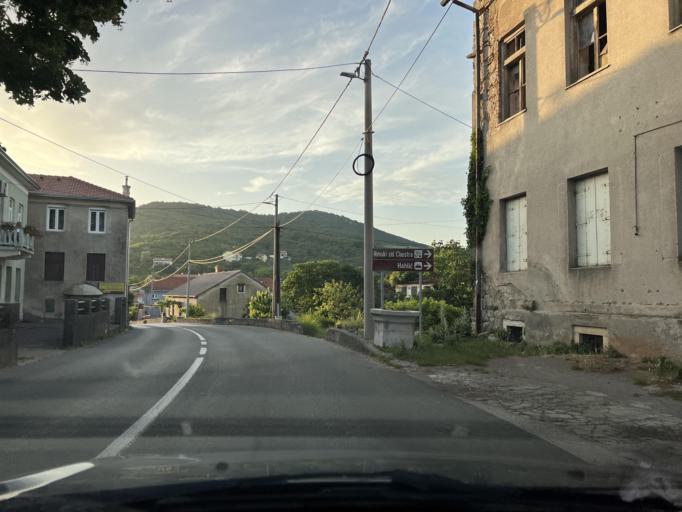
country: HR
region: Primorsko-Goranska
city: Drazice
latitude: 45.3867
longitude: 14.4518
